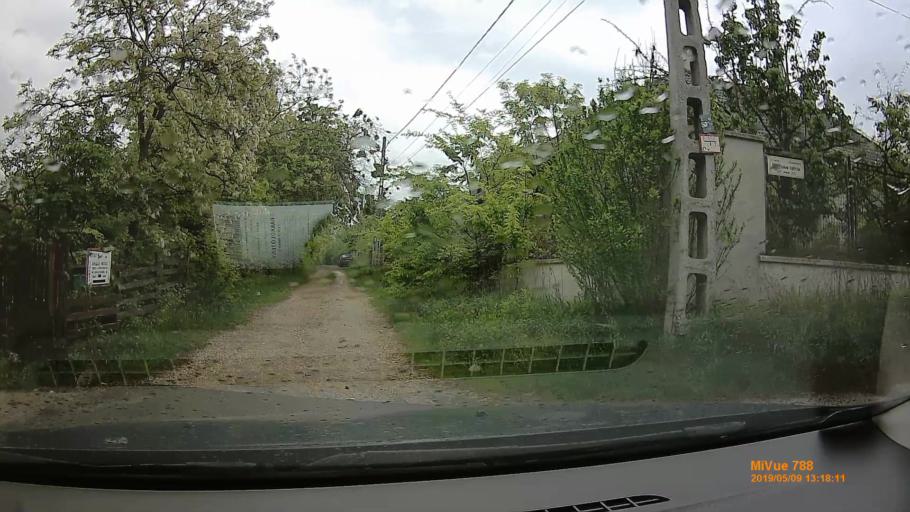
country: HU
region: Budapest
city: Budapest XVI. keruelet
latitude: 47.5410
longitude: 19.1866
